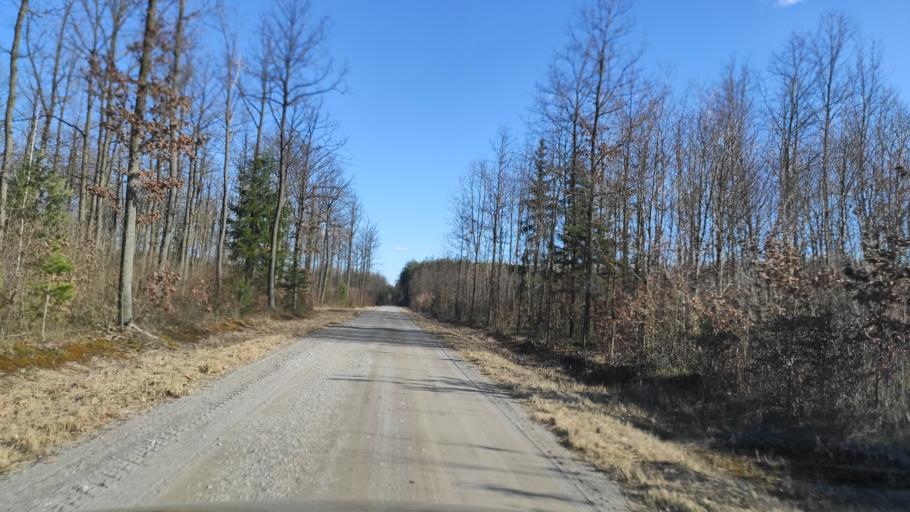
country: PL
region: Masovian Voivodeship
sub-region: Powiat radomski
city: Jedlnia-Letnisko
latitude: 51.4516
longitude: 21.2855
